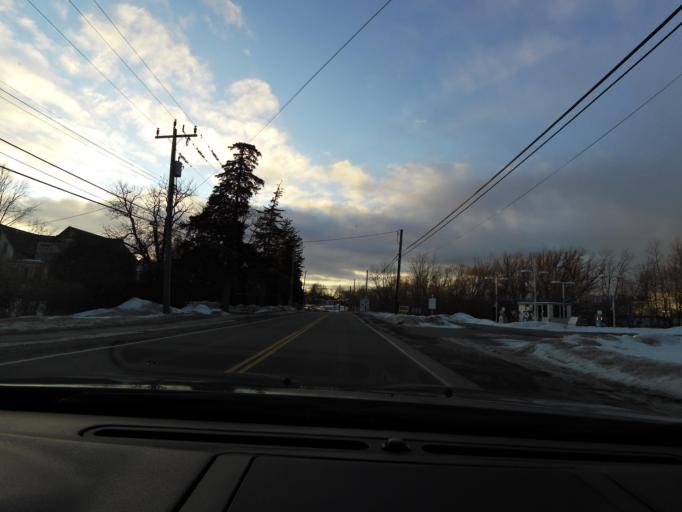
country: CA
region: Ontario
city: Hamilton
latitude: 43.2073
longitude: -79.6386
